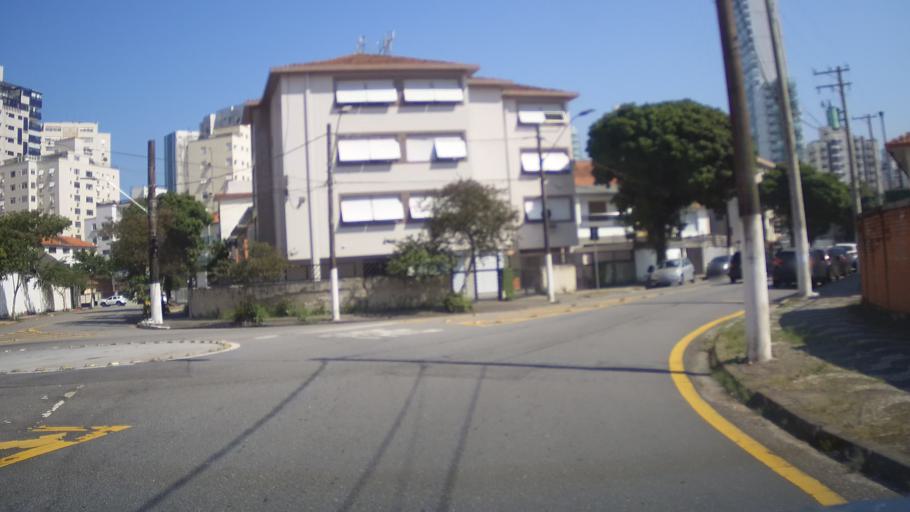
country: BR
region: Sao Paulo
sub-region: Santos
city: Santos
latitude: -23.9892
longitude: -46.3053
